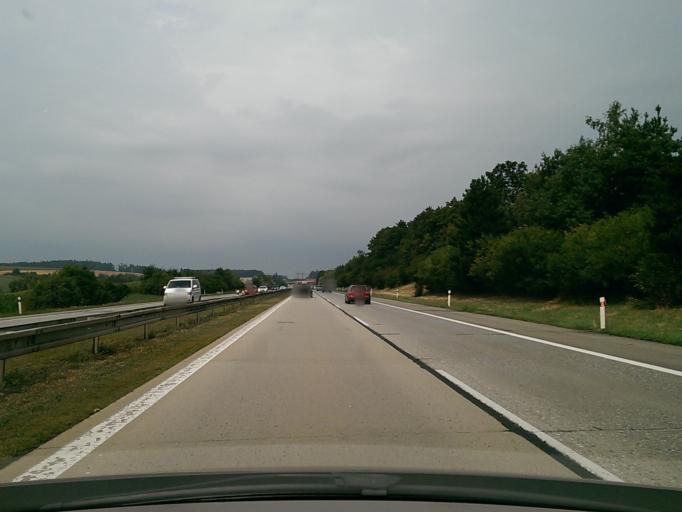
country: CZ
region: South Moravian
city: Ricany
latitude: 49.2484
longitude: 16.3587
